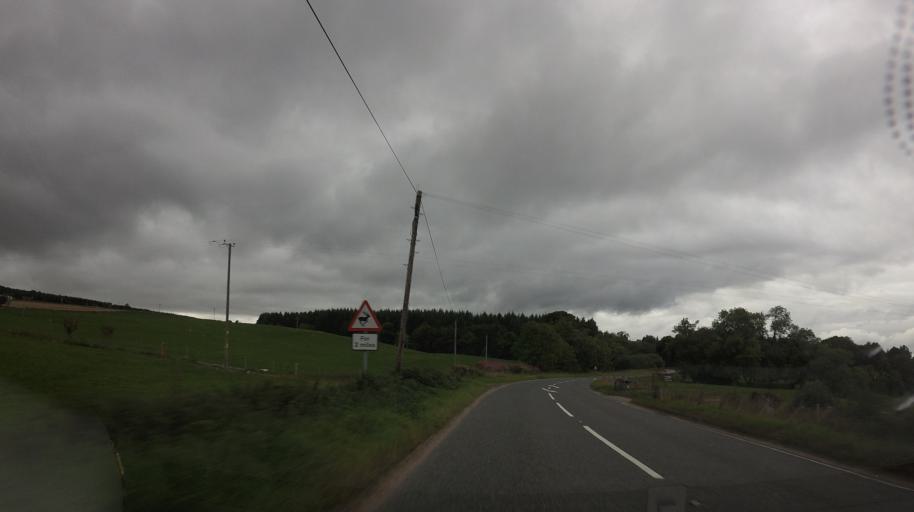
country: GB
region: Scotland
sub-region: Aberdeenshire
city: Torphins
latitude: 57.1917
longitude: -2.5776
